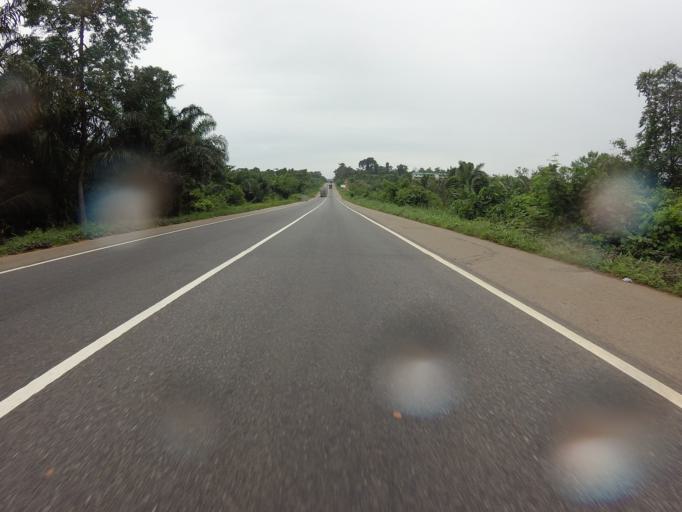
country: GH
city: Kibi
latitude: 6.1826
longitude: -0.4718
